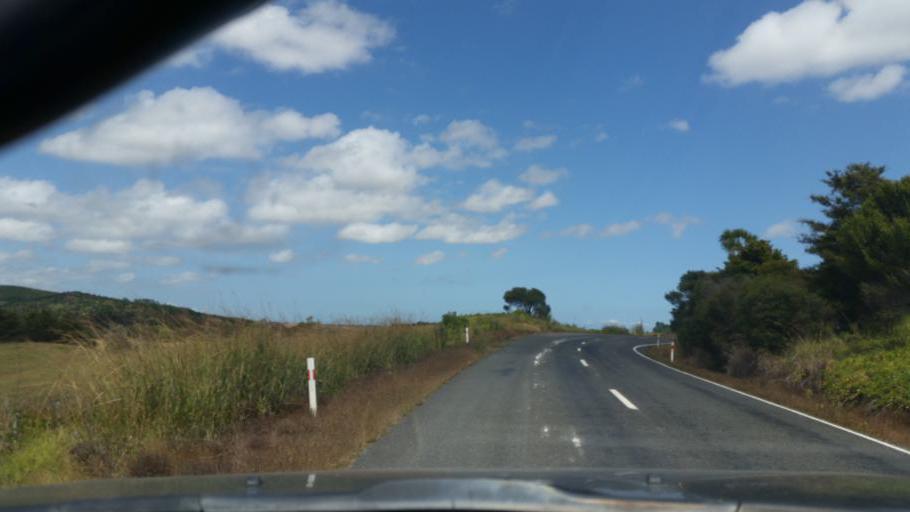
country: NZ
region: Northland
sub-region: Kaipara District
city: Dargaville
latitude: -35.8803
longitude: 173.8457
